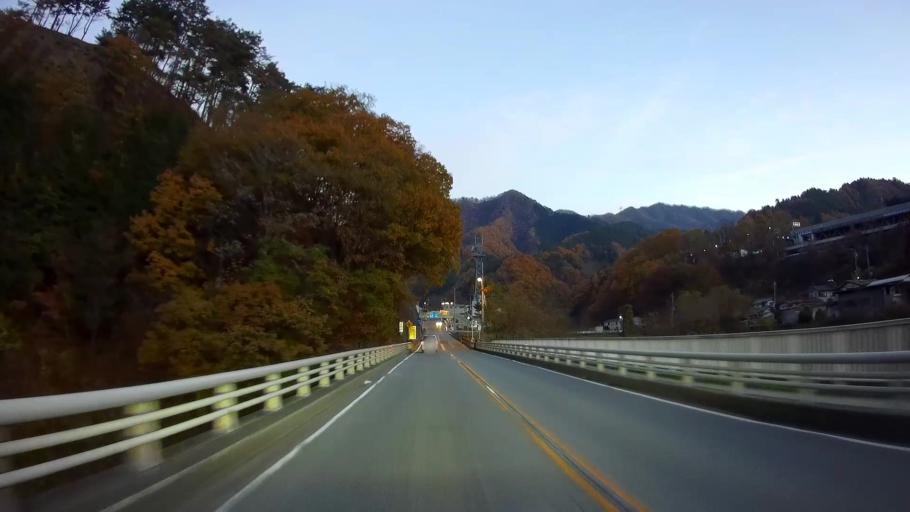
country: JP
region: Yamanashi
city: Enzan
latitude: 35.6417
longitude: 138.7738
